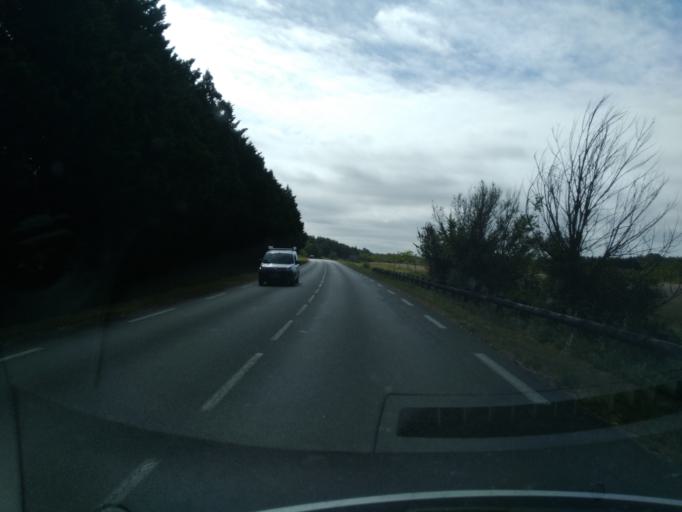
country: FR
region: Poitou-Charentes
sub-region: Departement de la Charente-Maritime
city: Chaillevette
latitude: 45.7100
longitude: -1.0644
